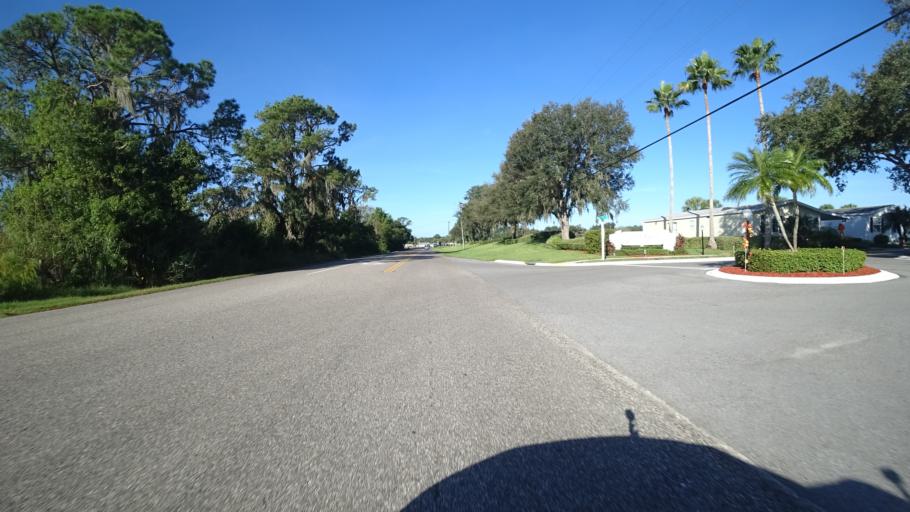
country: US
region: Florida
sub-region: Manatee County
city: Memphis
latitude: 27.5905
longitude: -82.5377
